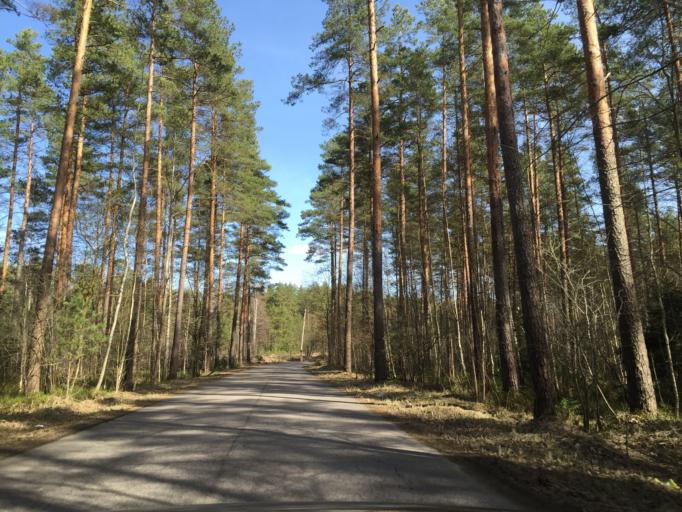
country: LV
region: Salaspils
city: Salaspils
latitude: 56.9189
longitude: 24.4005
